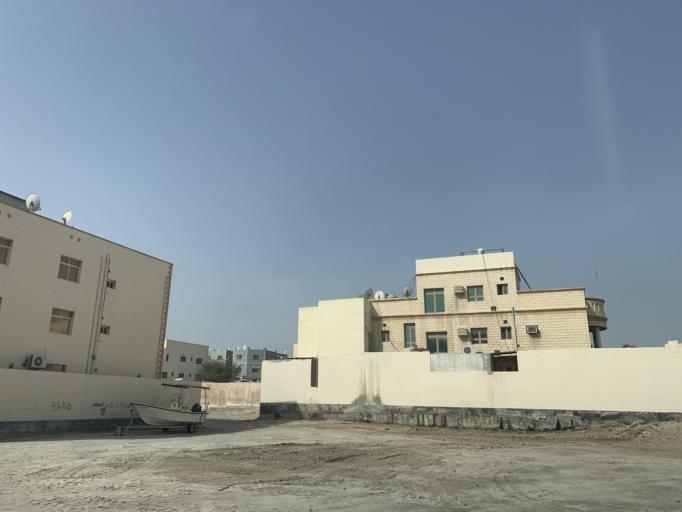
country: BH
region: Northern
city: Madinat `Isa
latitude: 26.1891
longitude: 50.5597
